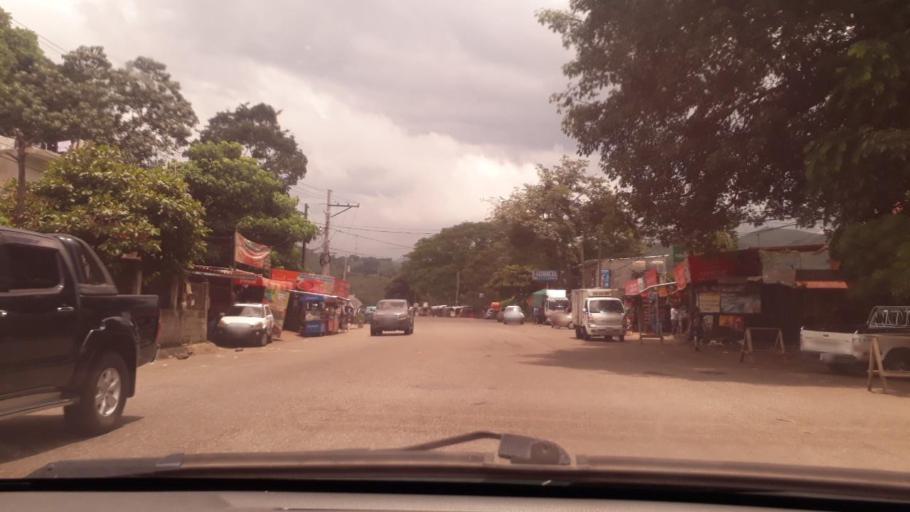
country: GT
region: Santa Rosa
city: Cuilapa
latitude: 14.2535
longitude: -90.2792
